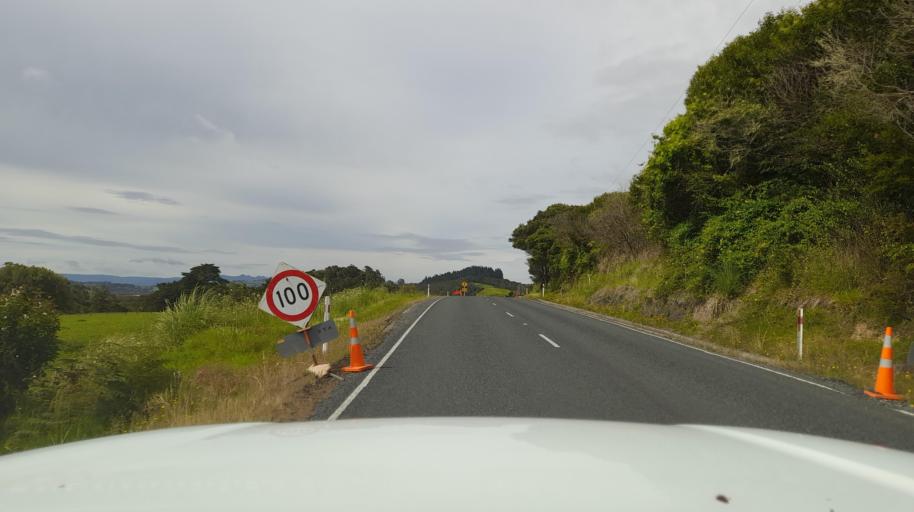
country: NZ
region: Northland
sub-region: Far North District
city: Taipa
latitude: -35.2640
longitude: 173.5251
